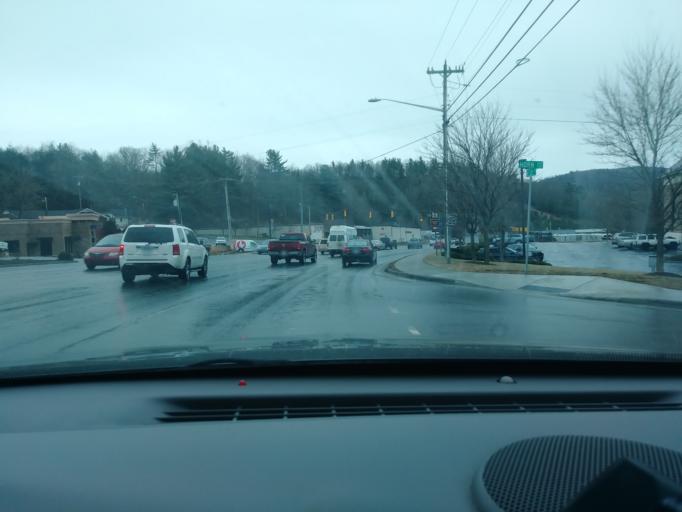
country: US
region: North Carolina
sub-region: Watauga County
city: Boone
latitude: 36.2109
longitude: -81.6673
